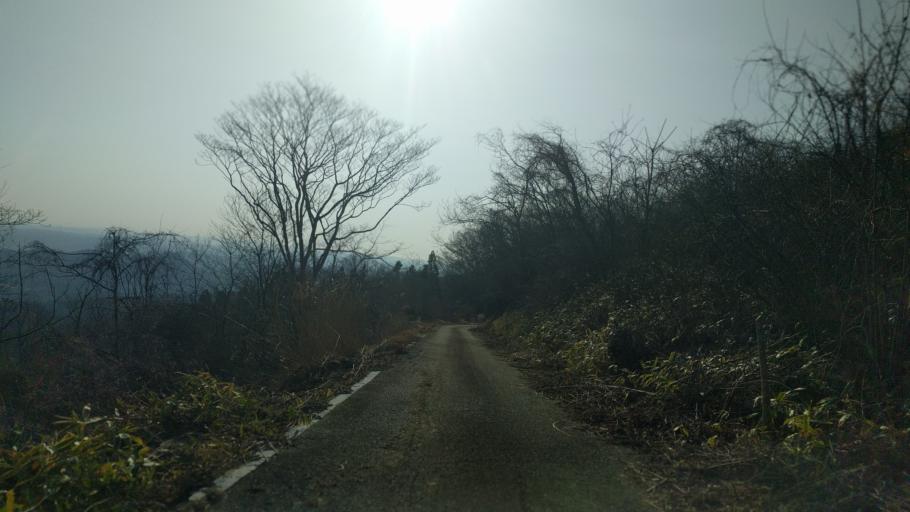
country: JP
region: Fukushima
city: Iwaki
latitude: 37.0384
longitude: 140.7937
